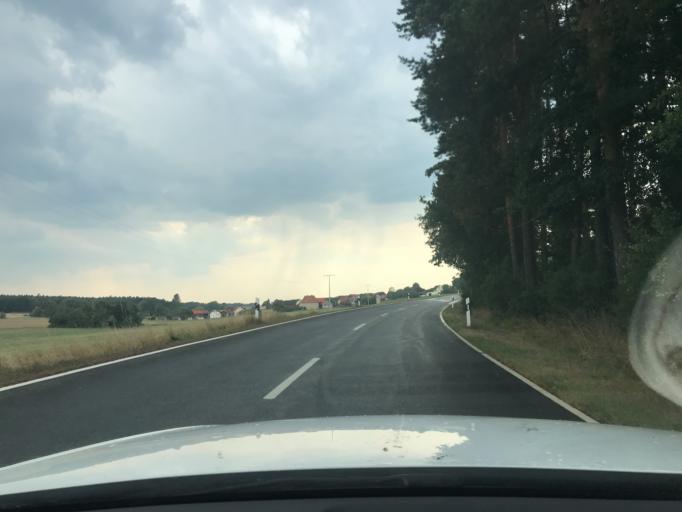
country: DE
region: Bavaria
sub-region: Upper Palatinate
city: Schlammersdorf
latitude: 49.7939
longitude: 11.7490
